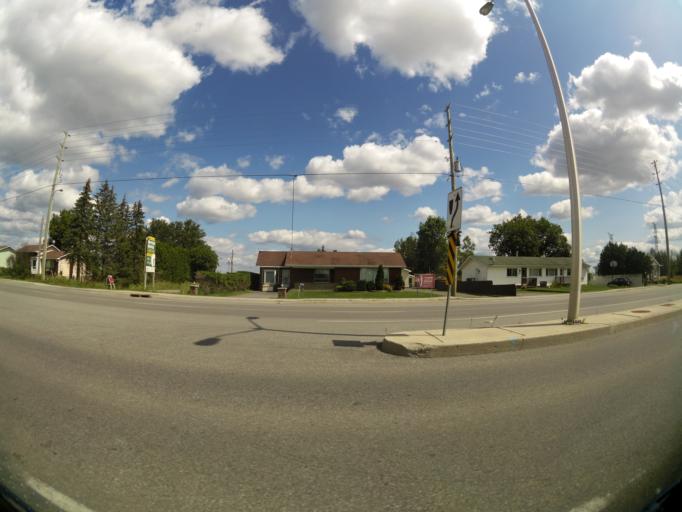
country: CA
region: Ontario
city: Ottawa
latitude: 45.4508
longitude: -75.5019
